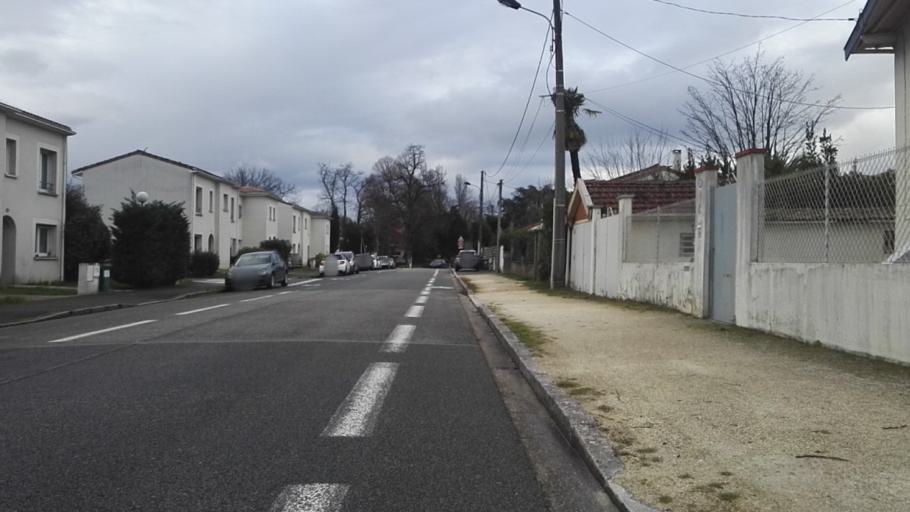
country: FR
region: Aquitaine
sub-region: Departement de la Gironde
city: Bruges
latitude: 44.8632
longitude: -0.6294
